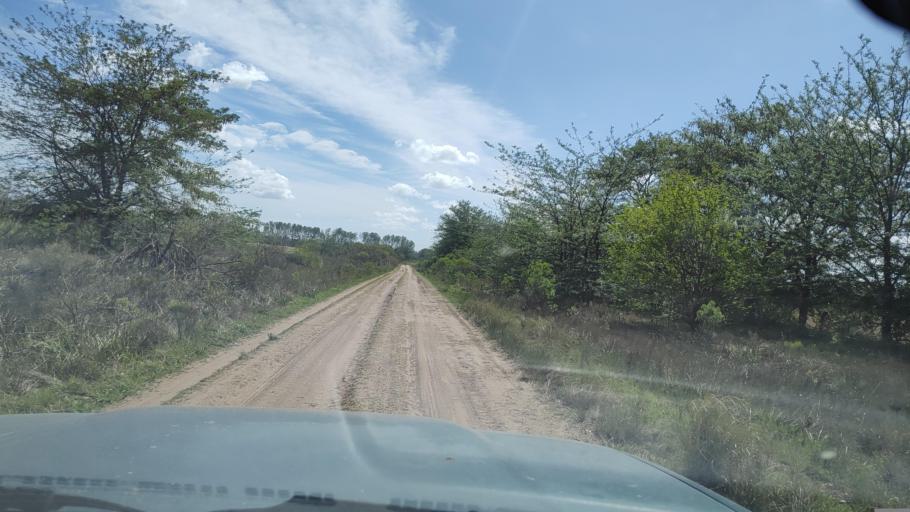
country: AR
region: Buenos Aires
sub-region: Partido de Lujan
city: Lujan
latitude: -34.5186
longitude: -59.1637
